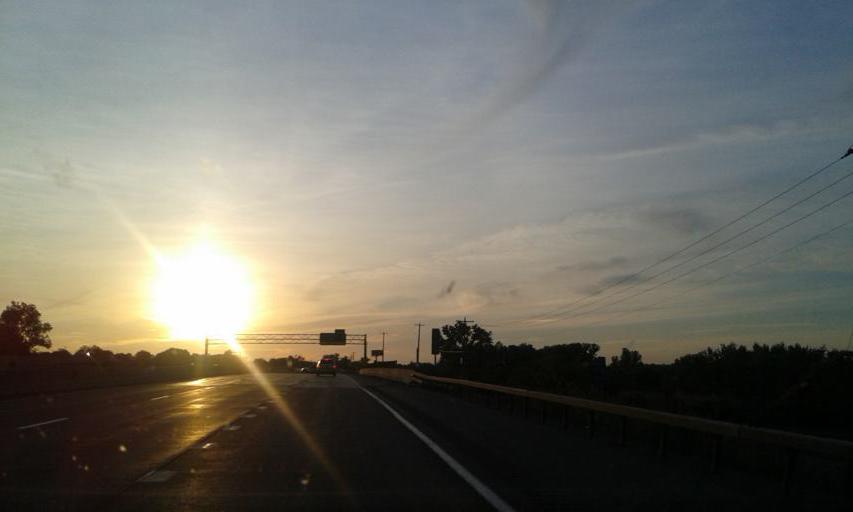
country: US
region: New York
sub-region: Onondaga County
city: Seneca Knolls
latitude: 43.1110
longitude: -76.2637
